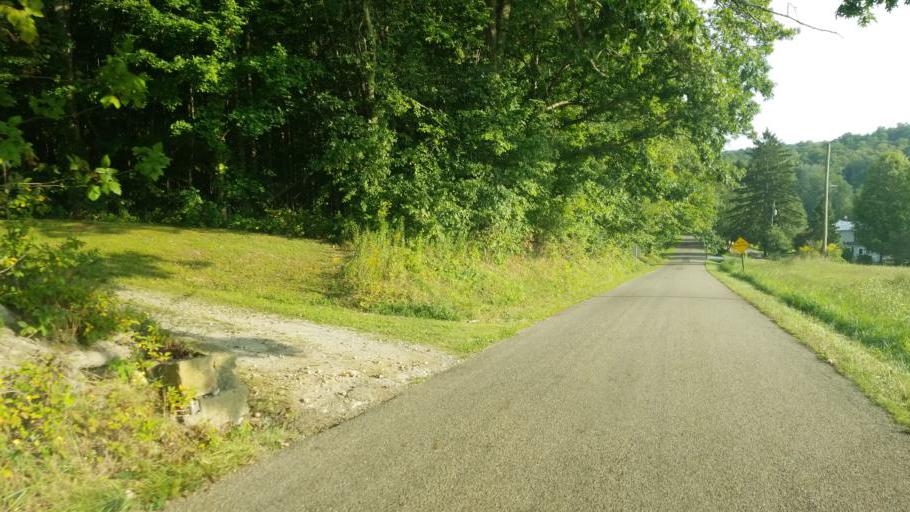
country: US
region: Ohio
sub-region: Sandusky County
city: Bellville
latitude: 40.6416
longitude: -82.4870
